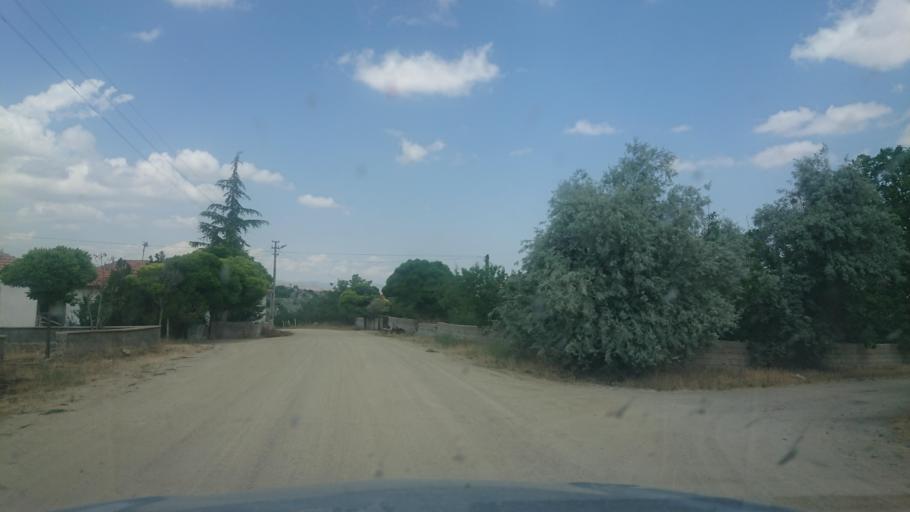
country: TR
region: Aksaray
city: Agacoren
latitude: 38.9322
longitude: 33.9570
